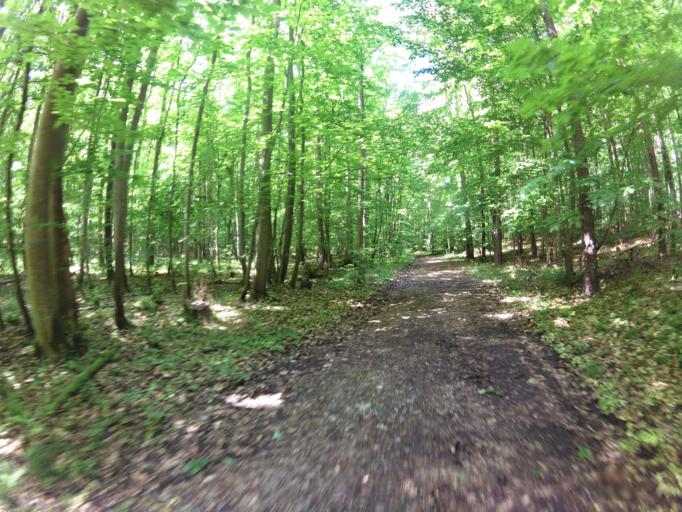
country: DE
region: Bavaria
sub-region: Regierungsbezirk Unterfranken
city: Uettingen
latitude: 49.7759
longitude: 9.7563
